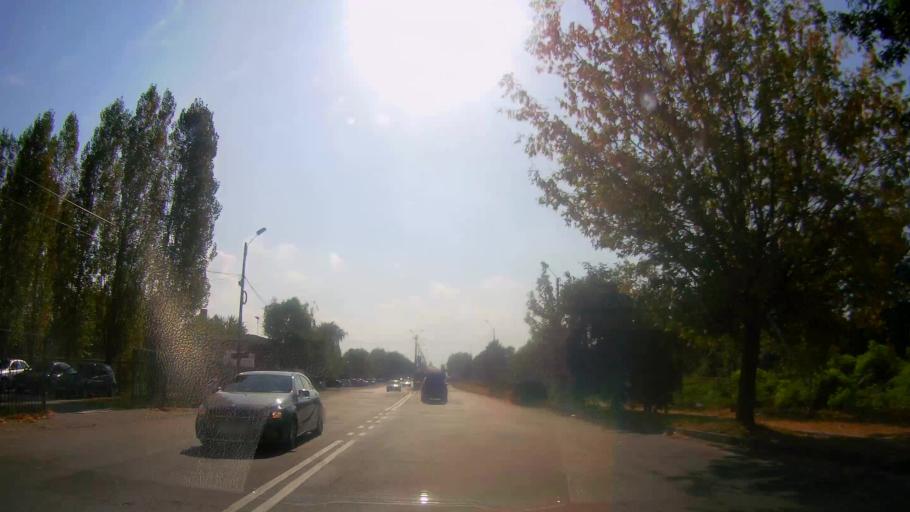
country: RO
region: Giurgiu
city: Giurgiu
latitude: 43.9093
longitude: 25.9791
